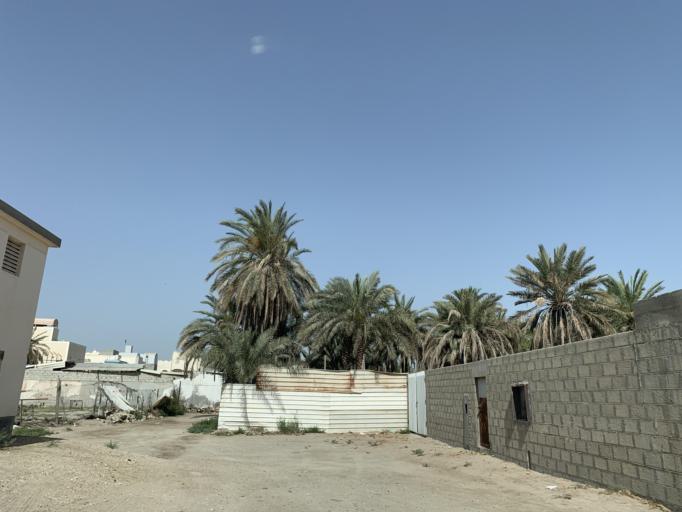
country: BH
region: Northern
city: Sitrah
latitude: 26.1466
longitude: 50.6079
